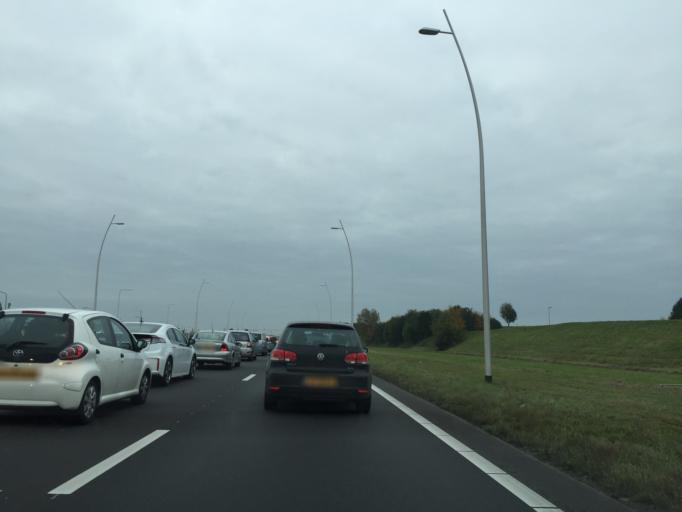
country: NL
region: North Brabant
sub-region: Gemeente Waalwijk
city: Waalwijk
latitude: 51.6814
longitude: 5.0451
